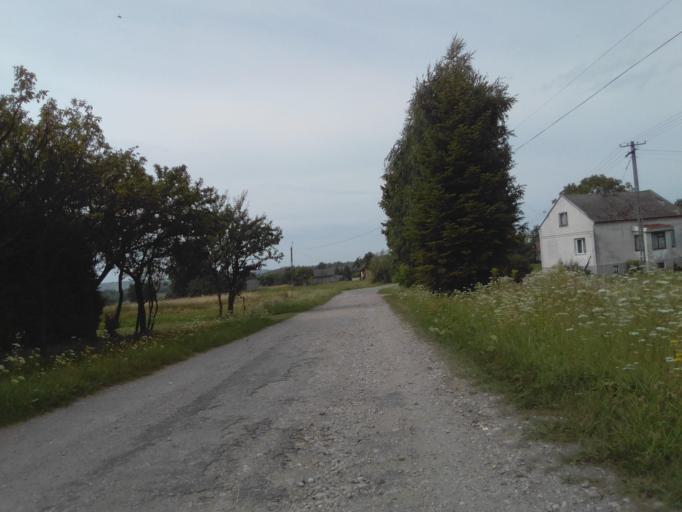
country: PL
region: Subcarpathian Voivodeship
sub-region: Powiat strzyzowski
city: Frysztak
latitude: 49.8781
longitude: 21.5319
